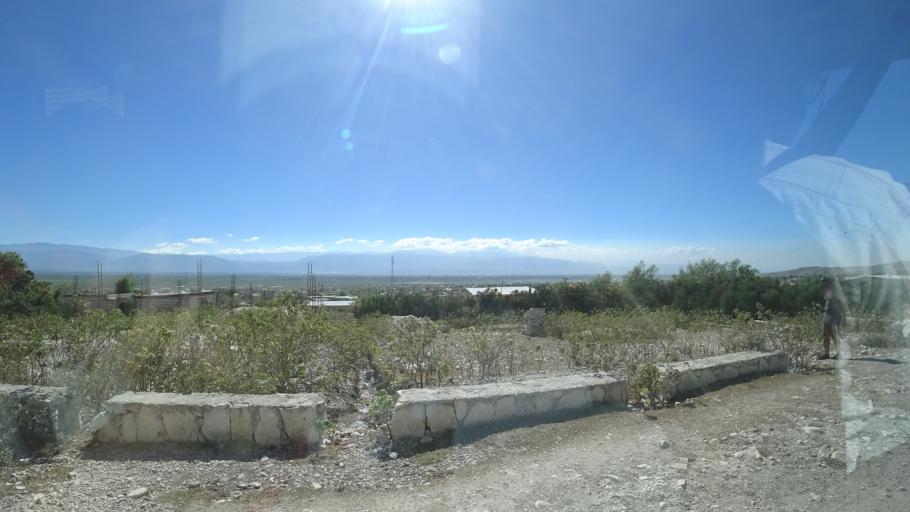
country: HT
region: Ouest
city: Croix des Bouquets
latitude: 18.6709
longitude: -72.2363
